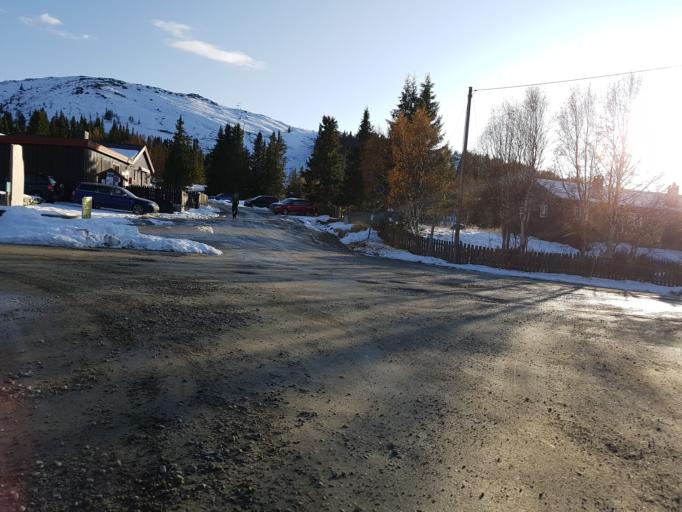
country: NO
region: Oppland
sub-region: Sel
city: Otta
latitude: 61.8088
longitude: 9.6835
